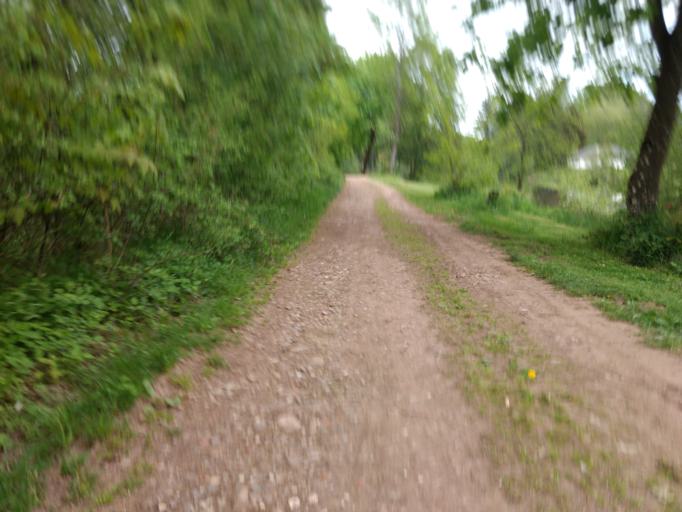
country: DE
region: Saarland
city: Nalbach
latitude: 49.3788
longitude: 6.8062
